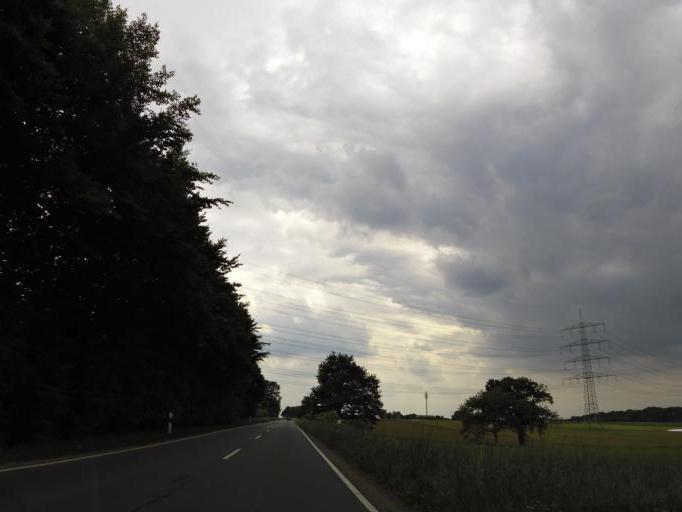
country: DE
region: Hesse
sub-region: Regierungsbezirk Darmstadt
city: Messel
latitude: 49.9511
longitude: 8.7428
